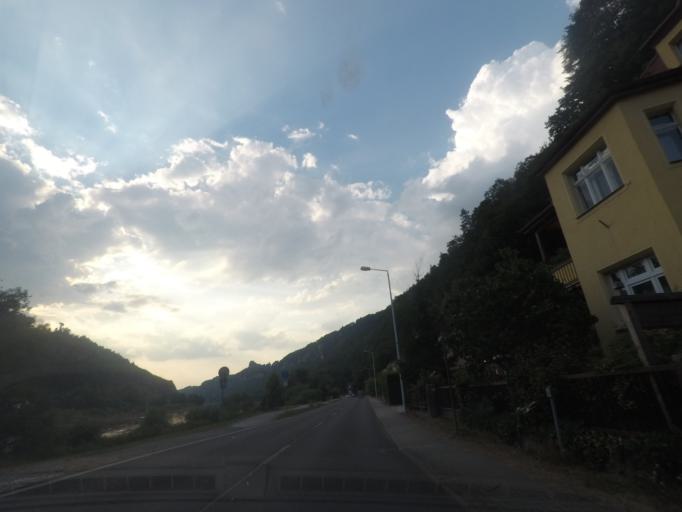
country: DE
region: Saxony
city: Bad Schandau
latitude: 50.8960
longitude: 14.2261
